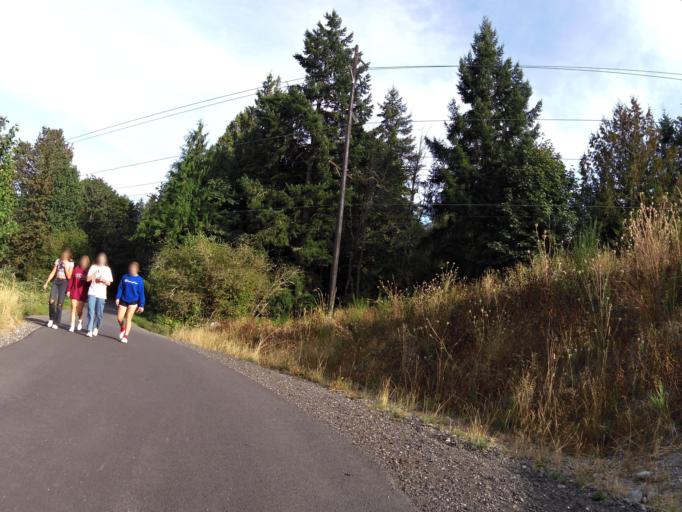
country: US
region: Washington
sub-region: Thurston County
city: Lacey
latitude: 46.9793
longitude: -122.8207
